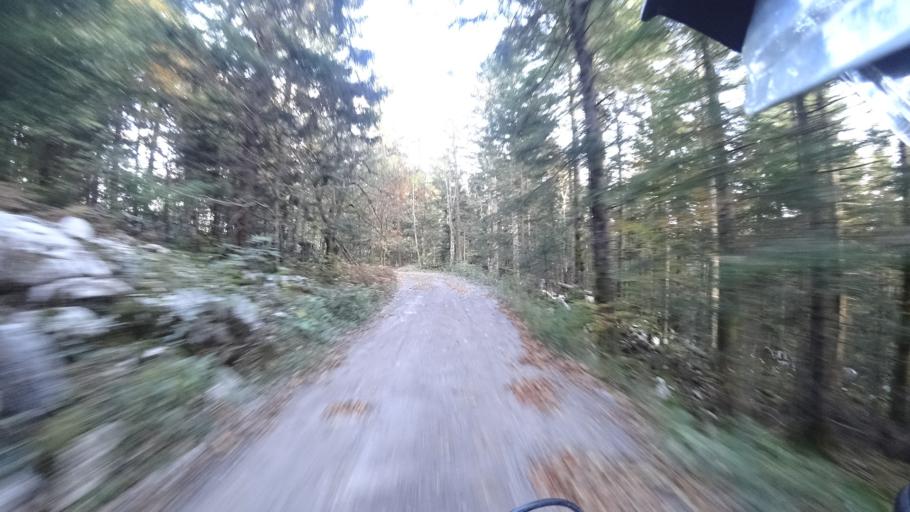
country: HR
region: Karlovacka
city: Plaski
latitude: 44.9622
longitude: 15.4360
